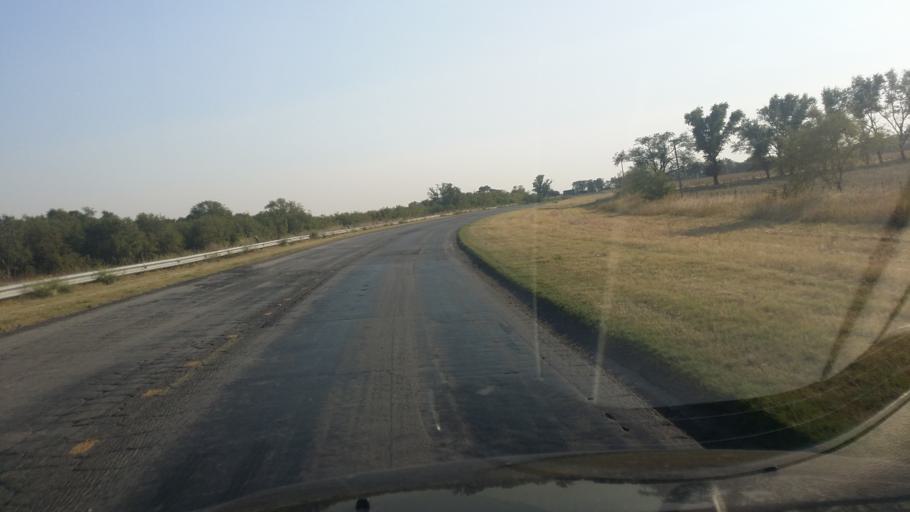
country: AR
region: La Pampa
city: Eduardo Castex
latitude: -35.9951
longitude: -64.2726
